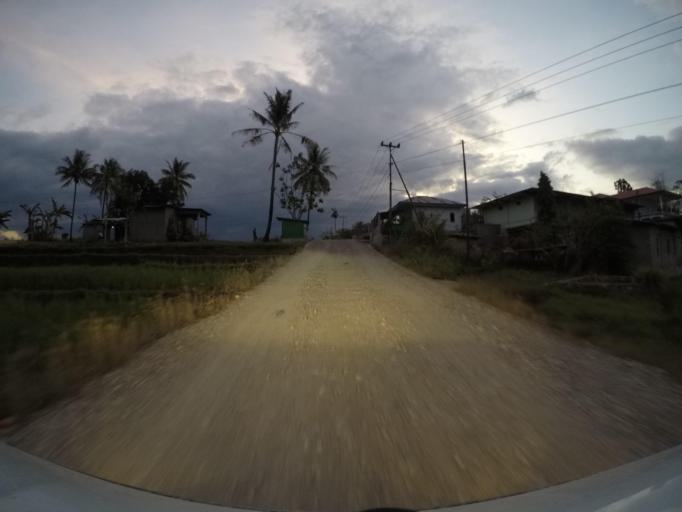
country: TL
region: Bobonaro
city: Maliana
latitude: -8.9805
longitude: 125.2171
